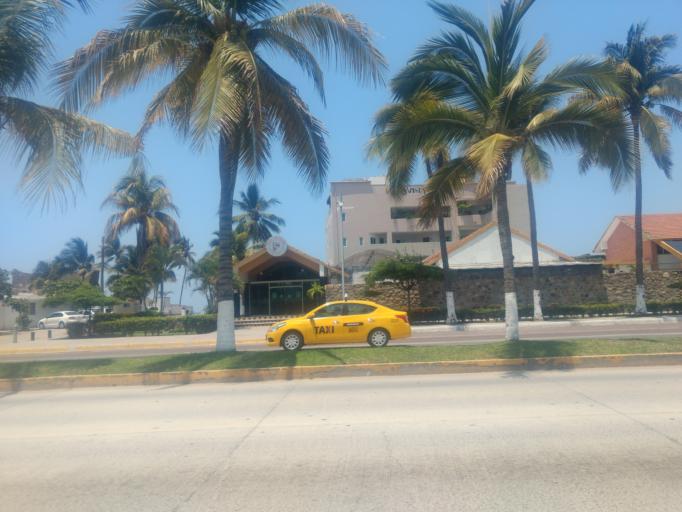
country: MX
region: Colima
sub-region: Manzanillo
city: Manzanillo
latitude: 19.0972
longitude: -104.3214
